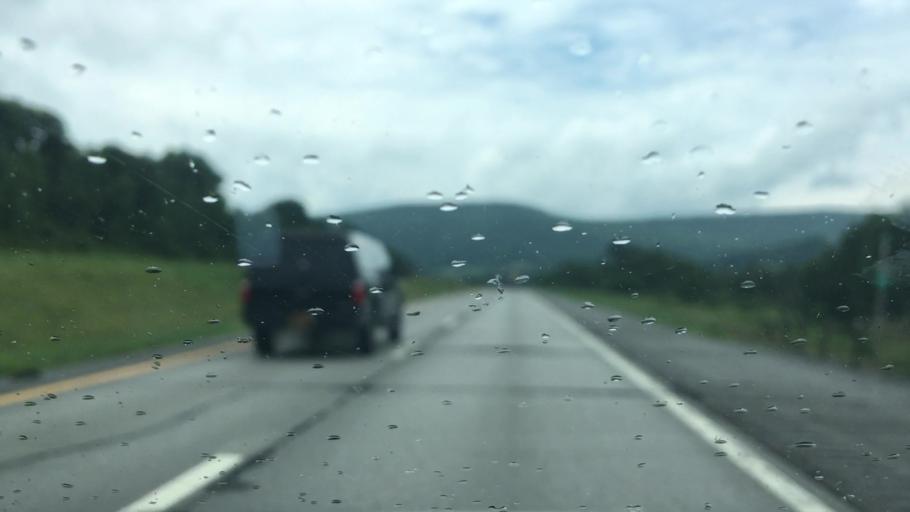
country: US
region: New York
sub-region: Otsego County
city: Worcester
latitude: 42.5872
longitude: -74.7436
